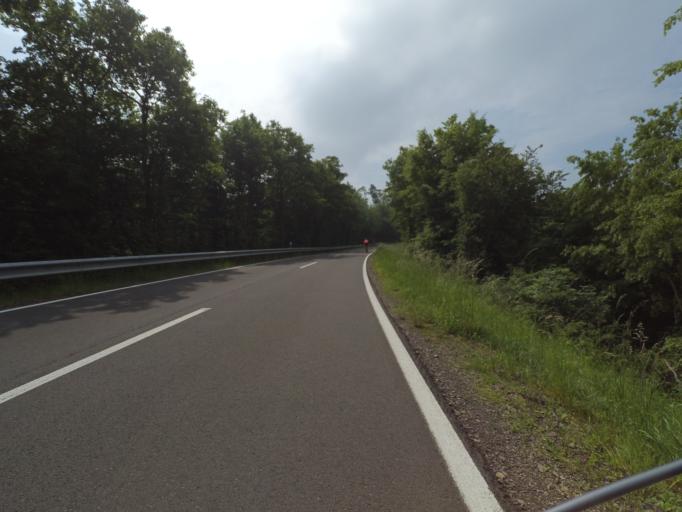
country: DE
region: Rheinland-Pfalz
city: Altstrimmig
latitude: 50.1133
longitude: 7.2939
